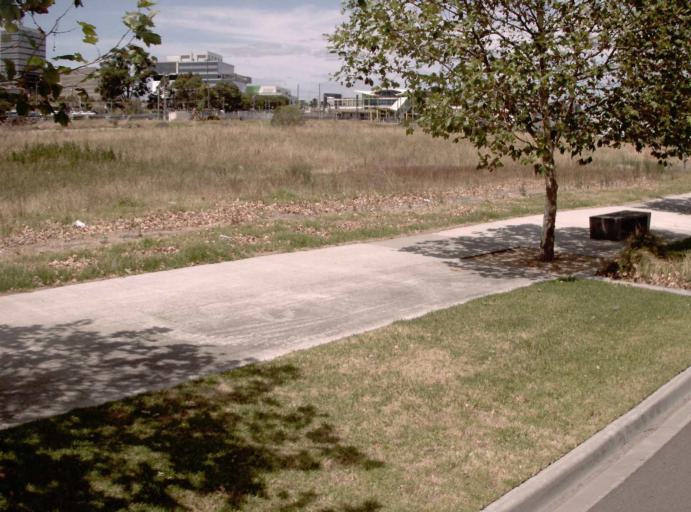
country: AU
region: Victoria
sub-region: Greater Dandenong
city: Dandenong
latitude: -37.9903
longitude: 145.2062
